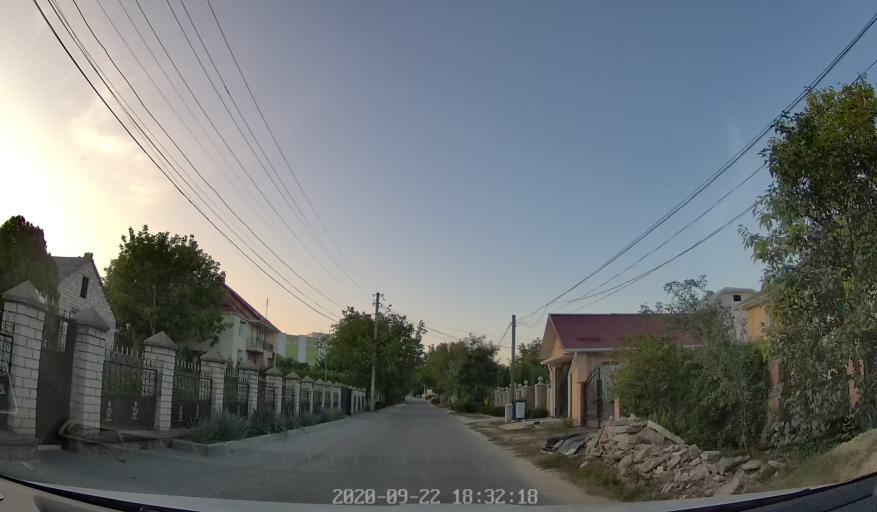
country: MD
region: Laloveni
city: Ialoveni
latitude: 46.9613
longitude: 28.7580
